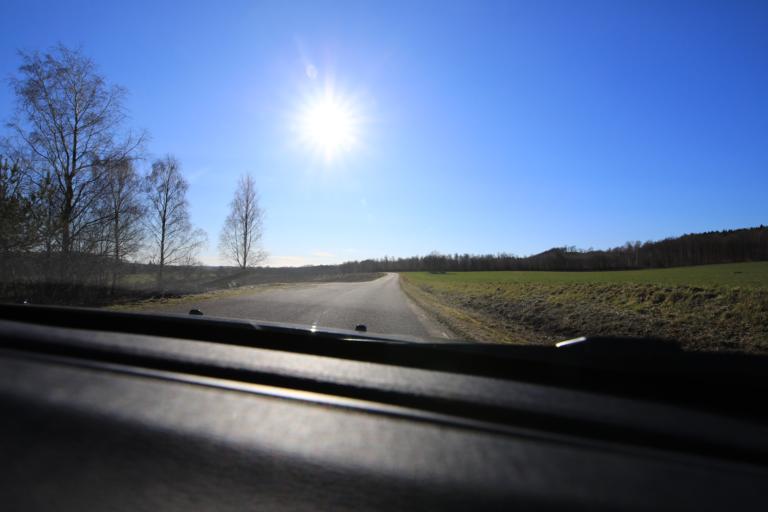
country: SE
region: Halland
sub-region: Varbergs Kommun
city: Tvaaker
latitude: 57.0669
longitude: 12.4662
